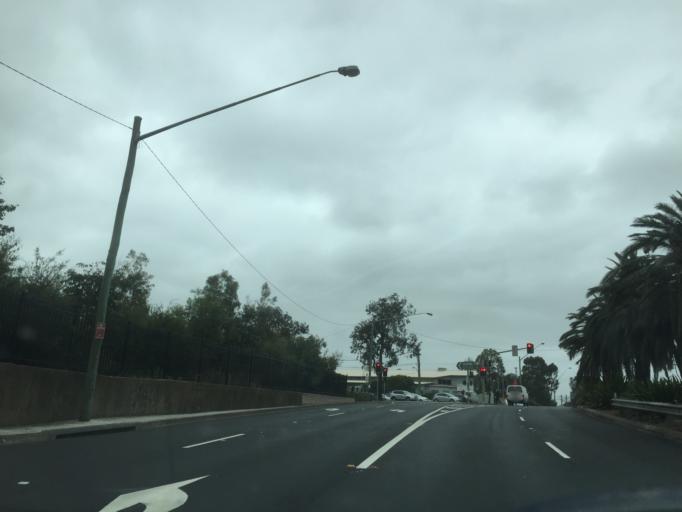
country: AU
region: New South Wales
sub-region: Blacktown
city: Blacktown
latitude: -33.7675
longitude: 150.9048
